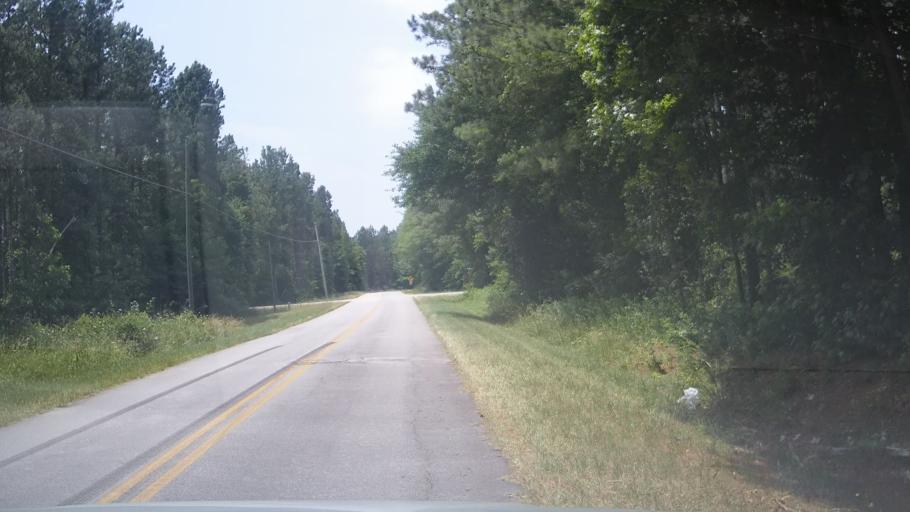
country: US
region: Georgia
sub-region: Hart County
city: Hartwell
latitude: 34.3465
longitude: -82.8987
